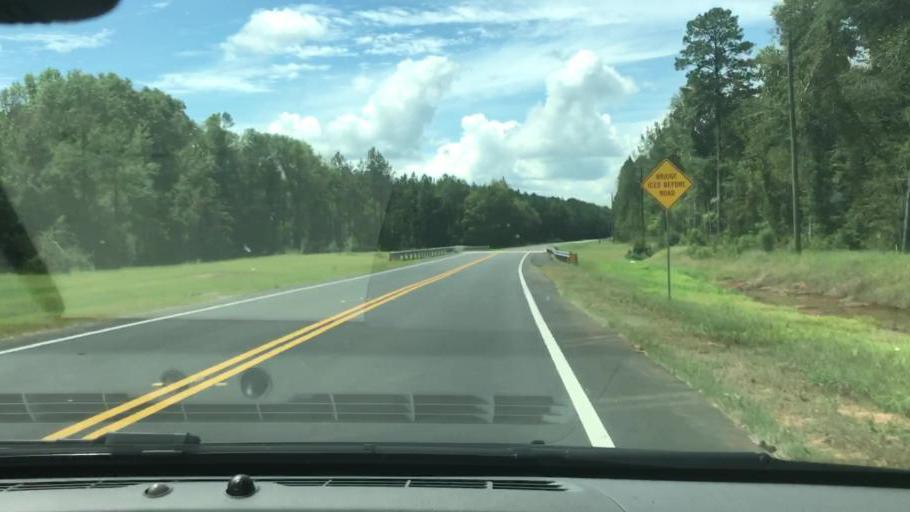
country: US
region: Georgia
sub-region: Stewart County
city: Lumpkin
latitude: 32.1410
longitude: -84.9351
